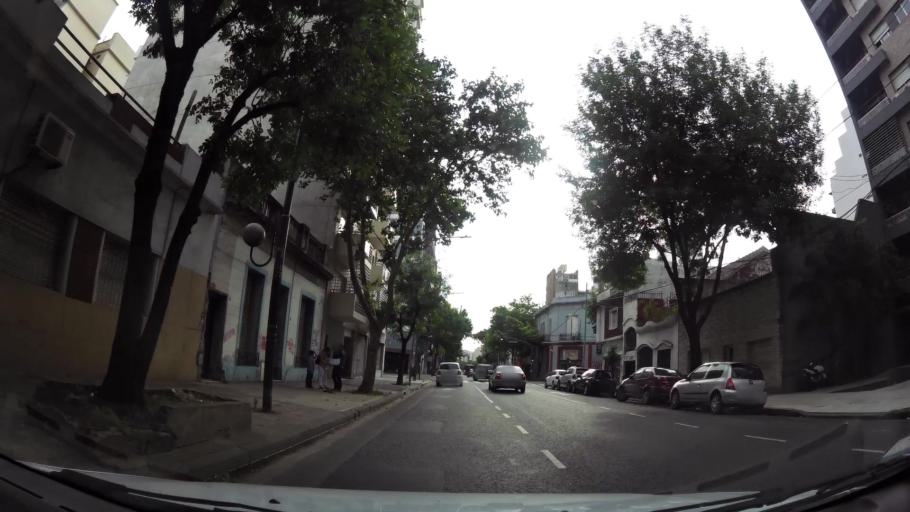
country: AR
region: Buenos Aires F.D.
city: Villa Santa Rita
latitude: -34.6330
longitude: -58.4667
